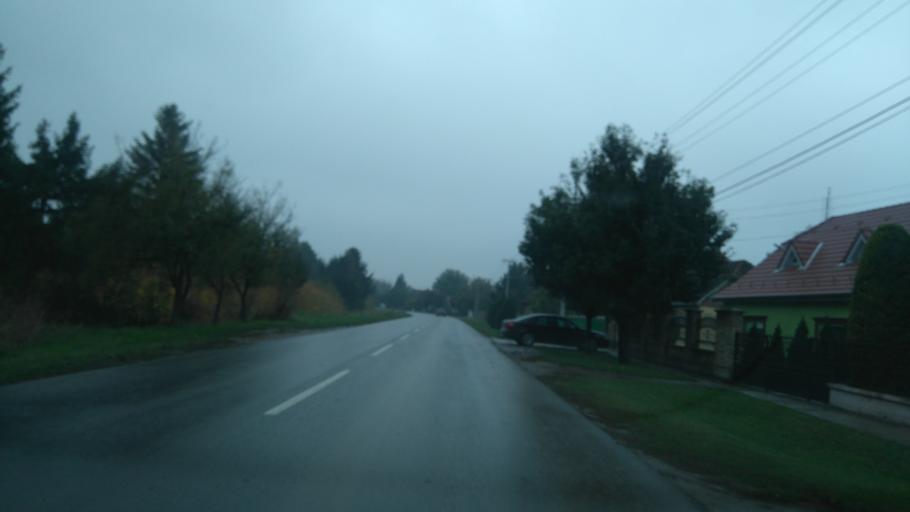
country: RS
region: Autonomna Pokrajina Vojvodina
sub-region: Juznobacki Okrug
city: Becej
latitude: 45.6421
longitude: 20.0281
